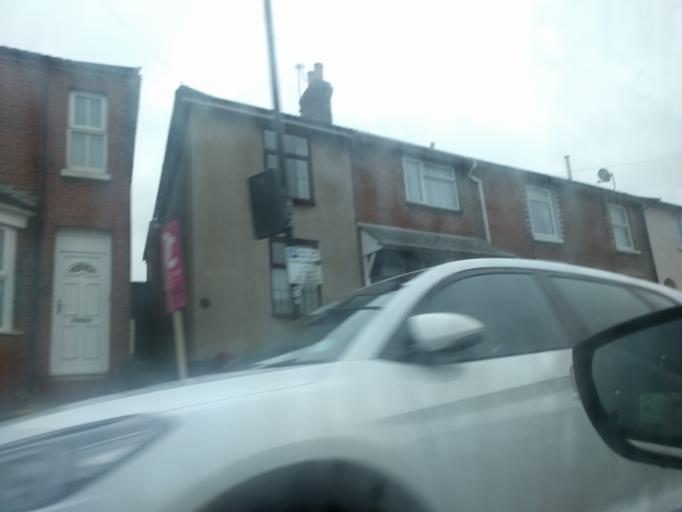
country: GB
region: England
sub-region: Southampton
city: Southampton
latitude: 50.9128
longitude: -1.4256
